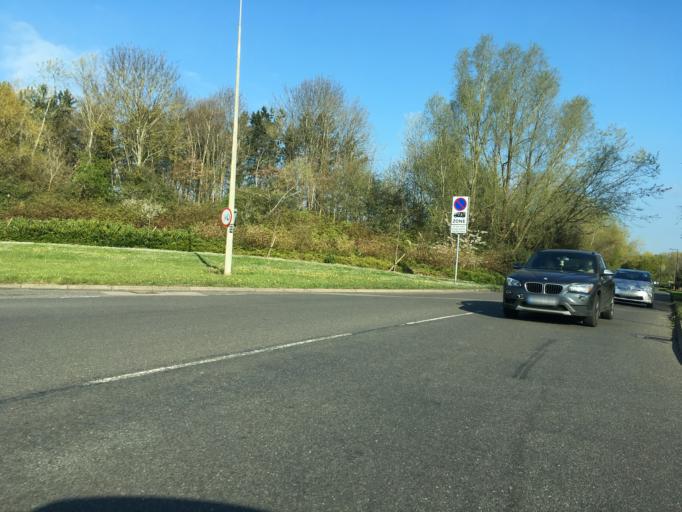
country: GB
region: England
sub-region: Milton Keynes
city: Newport Pagnell
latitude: 52.0653
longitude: -0.7273
